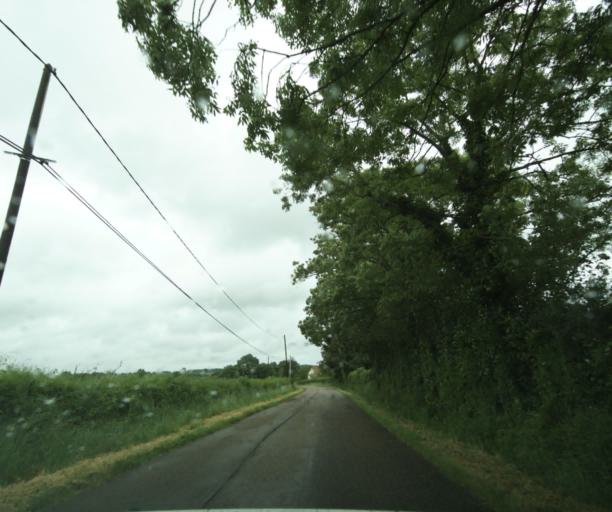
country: FR
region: Bourgogne
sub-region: Departement de Saone-et-Loire
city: Charolles
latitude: 46.4618
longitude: 4.4370
